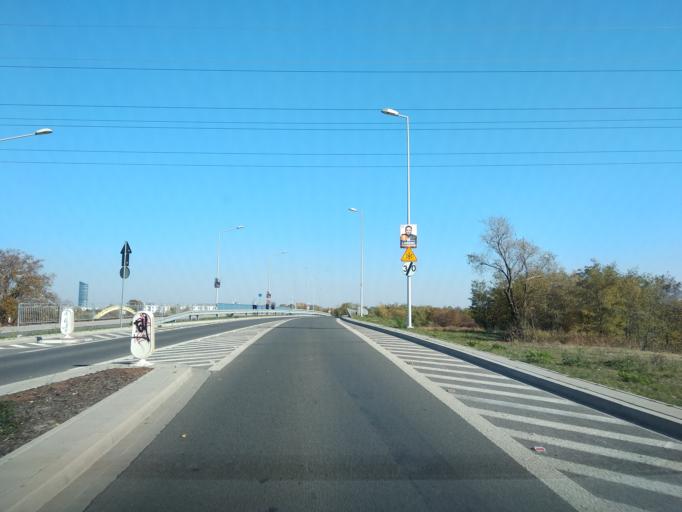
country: PL
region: Lower Silesian Voivodeship
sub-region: Powiat wroclawski
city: Bielany Wroclawskie
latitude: 51.0769
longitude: 16.9808
